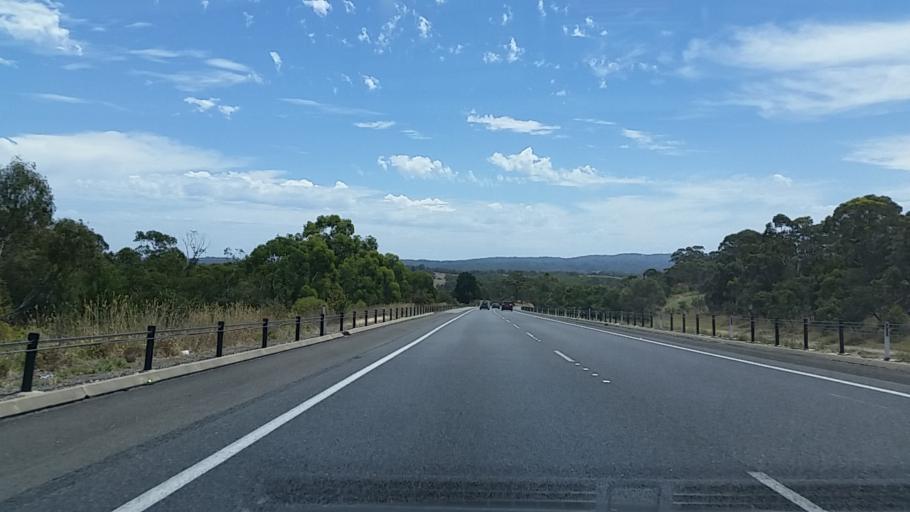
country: AU
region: South Australia
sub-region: Mount Barker
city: Little Hampton
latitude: -35.0495
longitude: 138.8261
